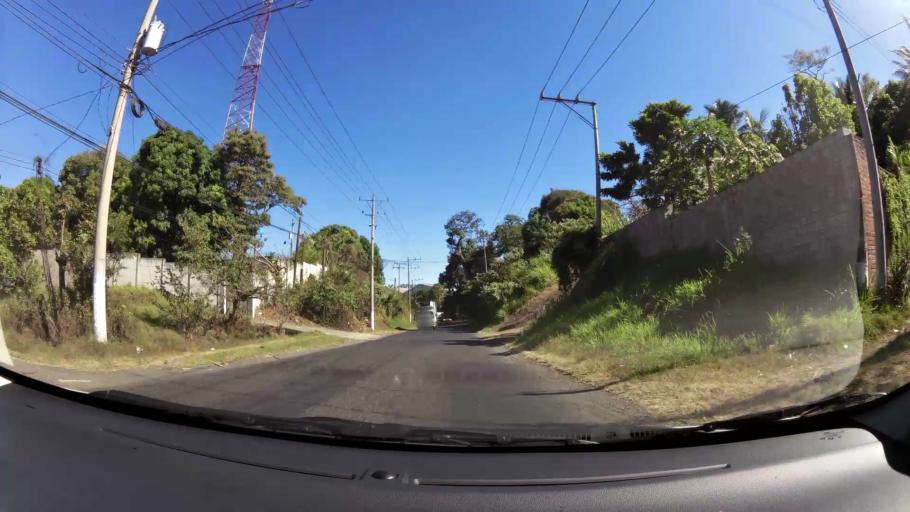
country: SV
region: La Libertad
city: San Juan Opico
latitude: 13.8112
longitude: -89.3565
